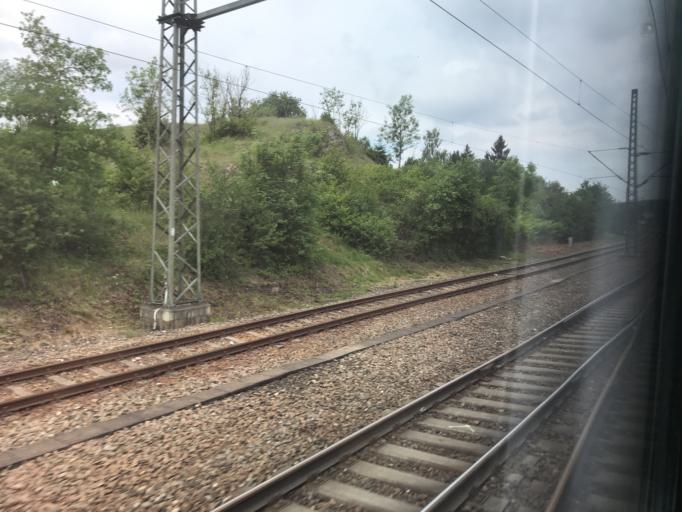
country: DE
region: Baden-Wuerttemberg
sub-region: Tuebingen Region
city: Amstetten
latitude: 48.5717
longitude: 9.8768
